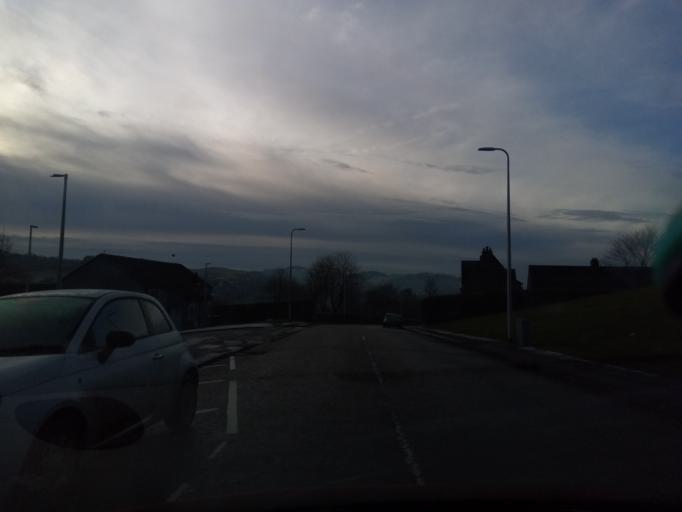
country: GB
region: Scotland
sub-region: The Scottish Borders
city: Hawick
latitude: 55.4340
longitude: -2.7744
